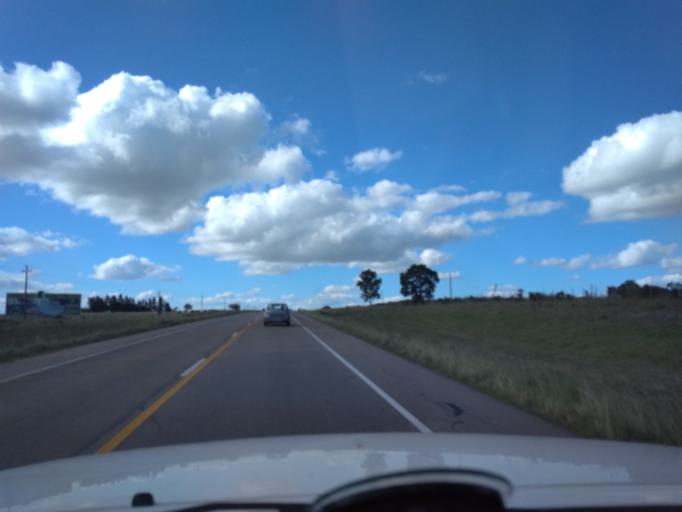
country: UY
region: Florida
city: Florida
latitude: -34.1793
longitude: -56.1916
